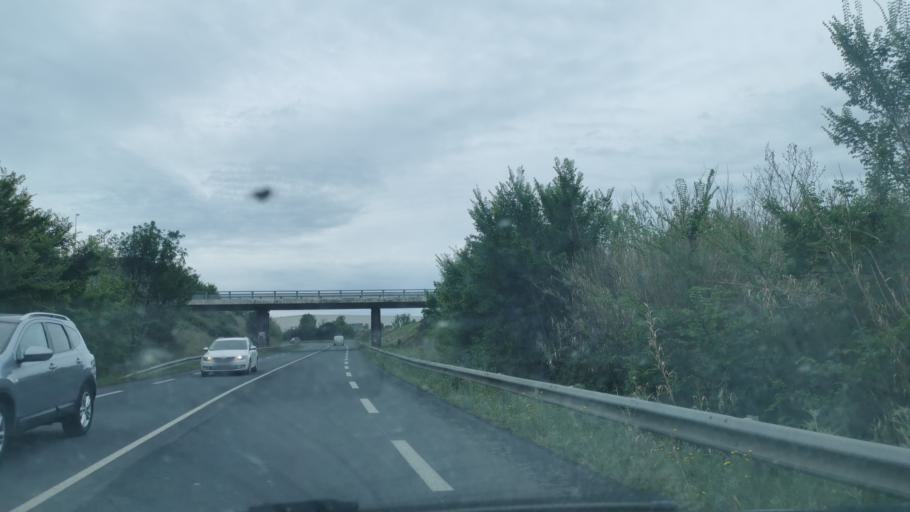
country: FR
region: Languedoc-Roussillon
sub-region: Departement de l'Herault
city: Gigean
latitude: 43.4924
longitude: 3.7011
